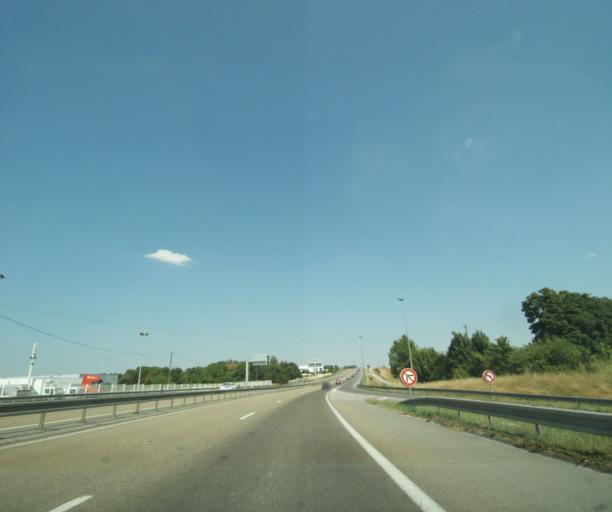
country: FR
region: Champagne-Ardenne
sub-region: Departement de la Marne
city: Chalons-en-Champagne
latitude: 48.9834
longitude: 4.3519
